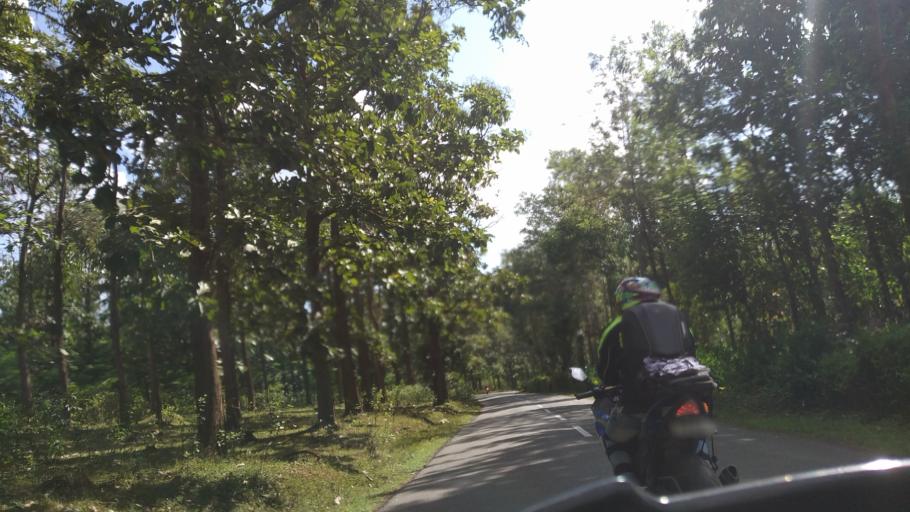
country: IN
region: Kerala
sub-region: Wayanad
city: Panamaram
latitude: 11.9372
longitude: 76.0648
